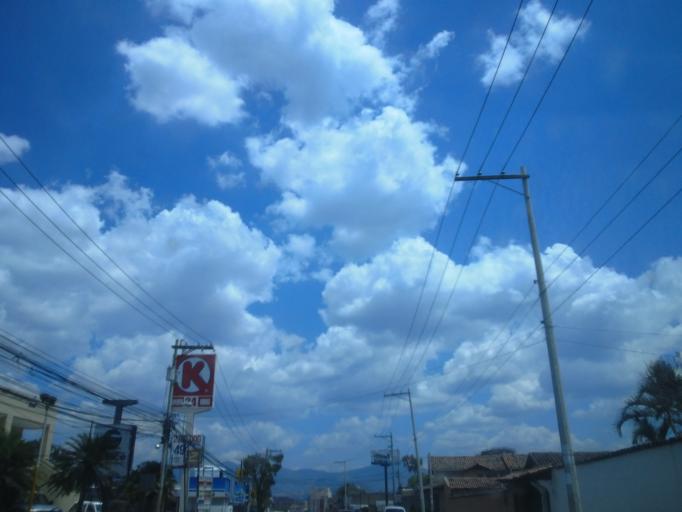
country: HN
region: Francisco Morazan
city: Tegucigalpa
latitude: 14.0600
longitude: -87.2278
